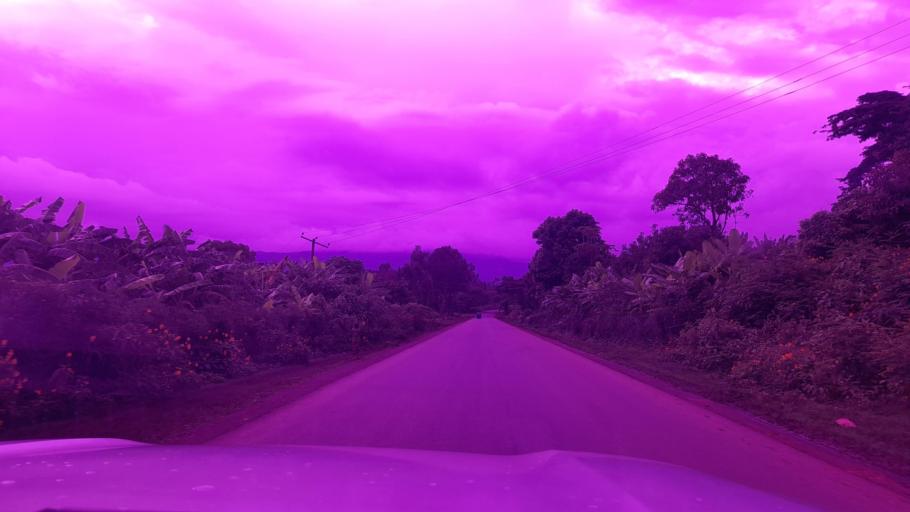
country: ET
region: Oromiya
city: Jima
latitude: 7.8903
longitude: 37.3899
